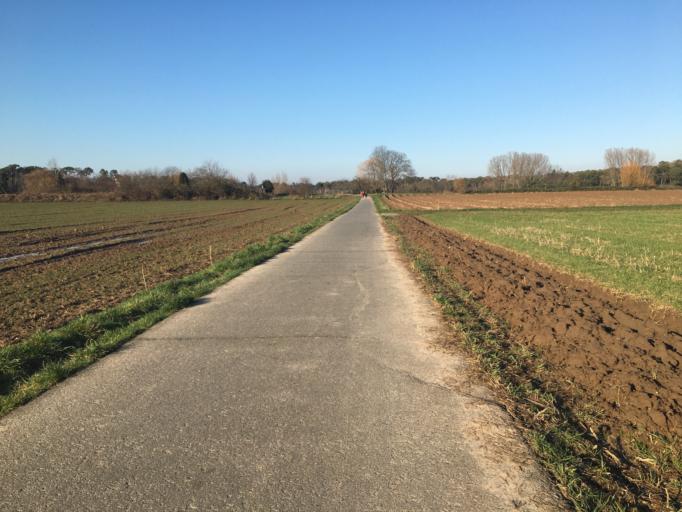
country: DE
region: Hesse
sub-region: Regierungsbezirk Darmstadt
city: Bickenbach
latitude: 49.7548
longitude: 8.6225
